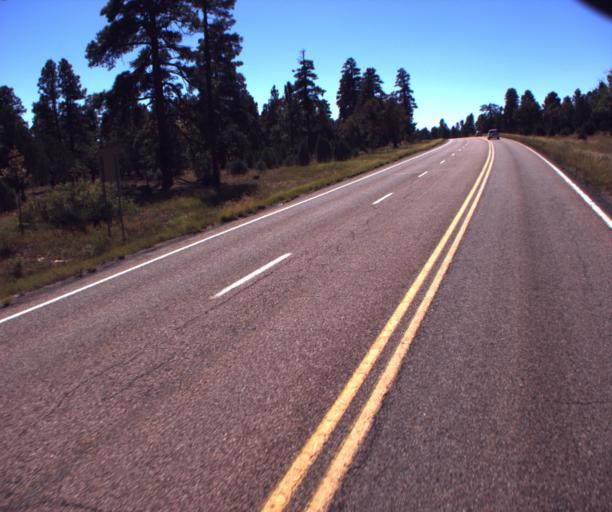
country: US
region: Arizona
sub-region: Navajo County
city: Heber-Overgaard
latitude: 34.3963
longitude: -110.6711
